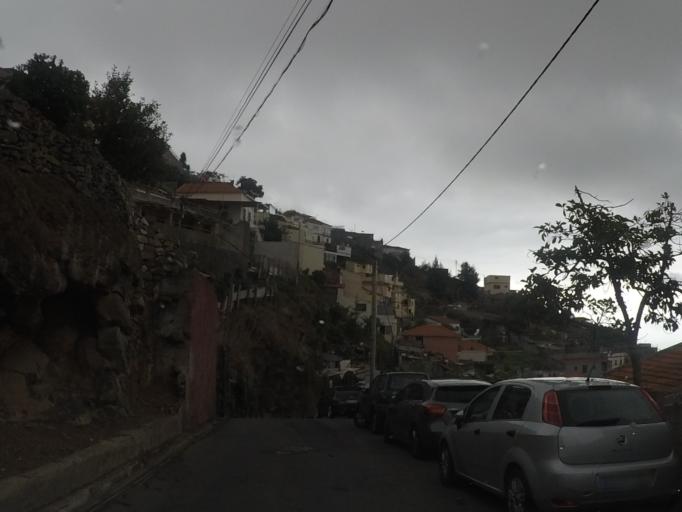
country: PT
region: Madeira
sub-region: Funchal
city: Nossa Senhora do Monte
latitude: 32.6734
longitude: -16.9138
